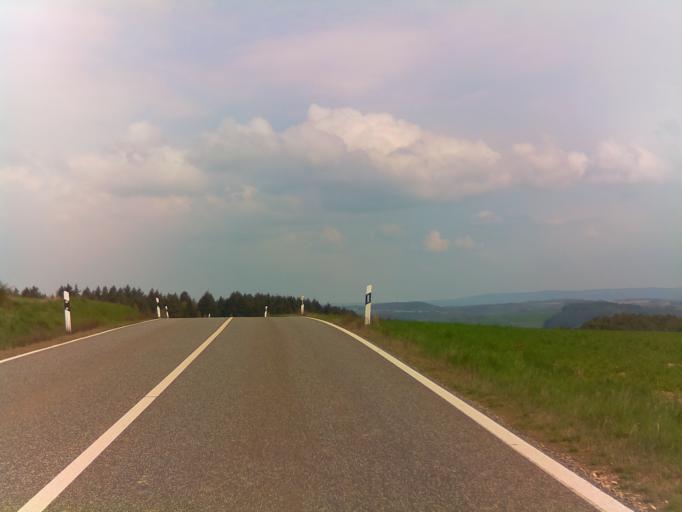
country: DE
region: Rheinland-Pfalz
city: Stipshausen
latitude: 49.8561
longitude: 7.3002
